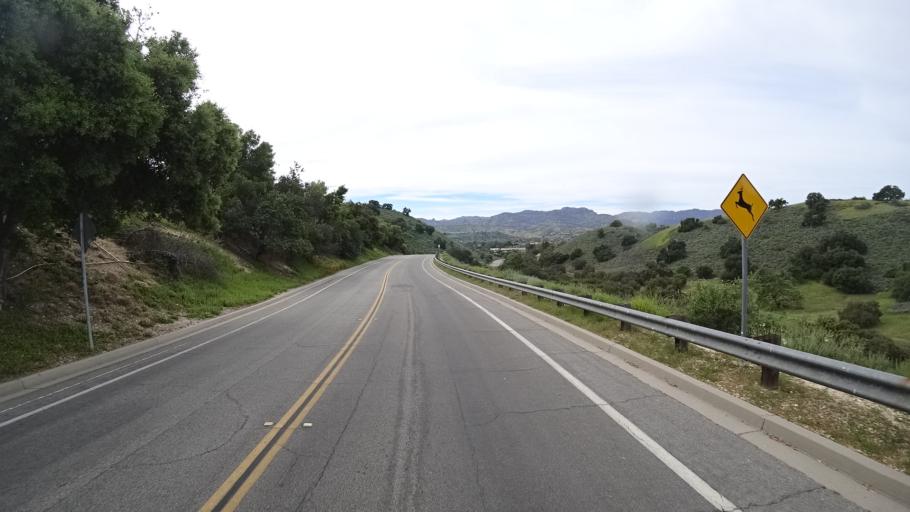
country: US
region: California
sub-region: Los Angeles County
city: Westlake Village
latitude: 34.1630
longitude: -118.8097
